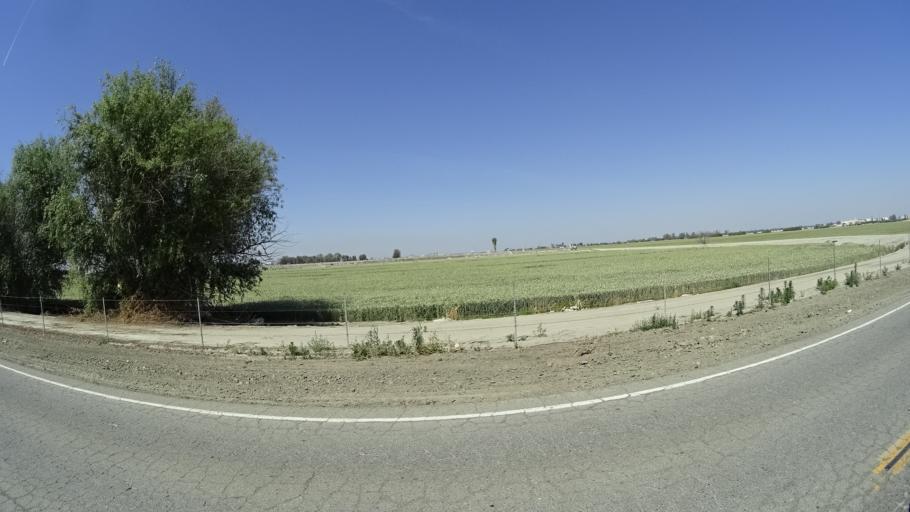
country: US
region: California
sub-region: Kings County
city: Corcoran
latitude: 36.0683
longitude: -119.5369
